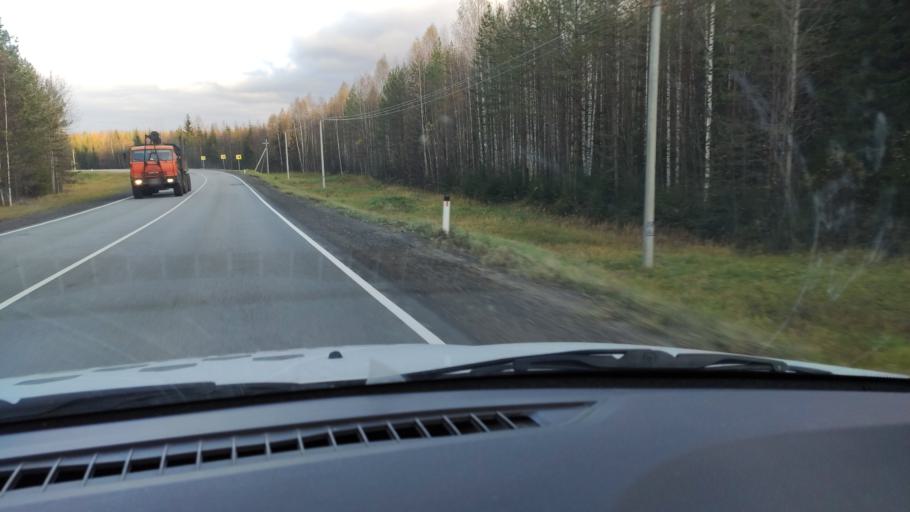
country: RU
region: Kirov
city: Belaya Kholunitsa
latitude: 58.9055
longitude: 51.0308
